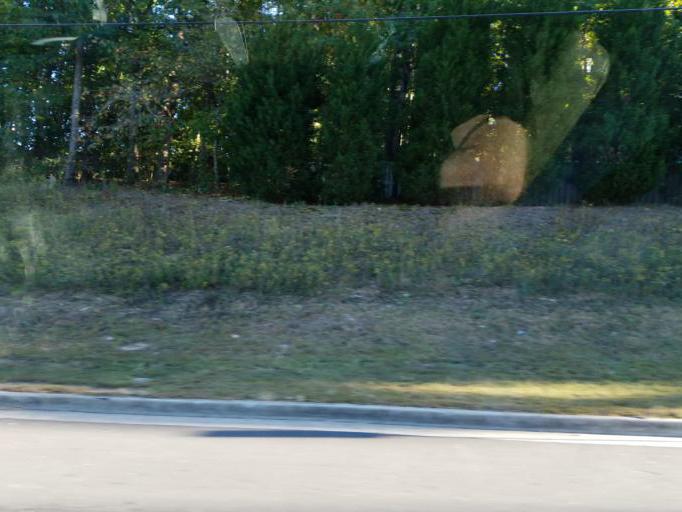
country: US
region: Georgia
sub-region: Fulton County
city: Roswell
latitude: 34.0100
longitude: -84.3800
